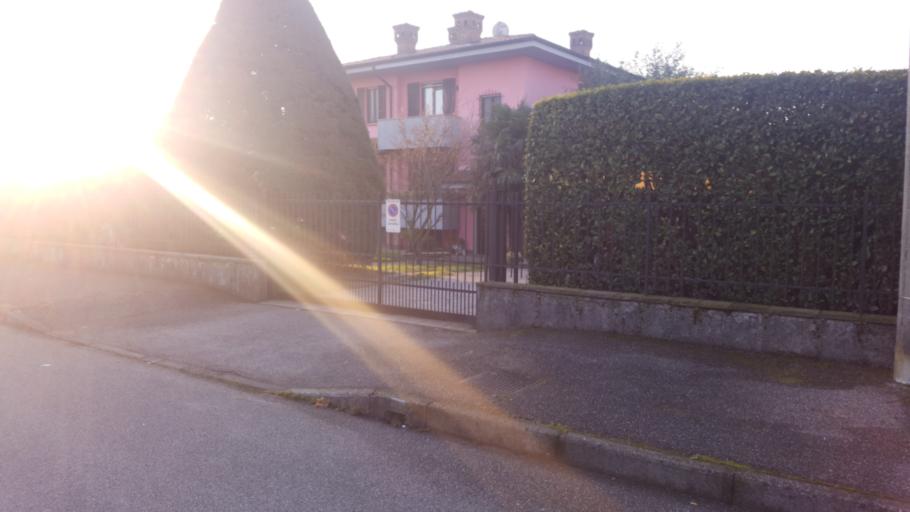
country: IT
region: Lombardy
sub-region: Citta metropolitana di Milano
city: Cassano d'Adda
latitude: 45.5259
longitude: 9.5007
